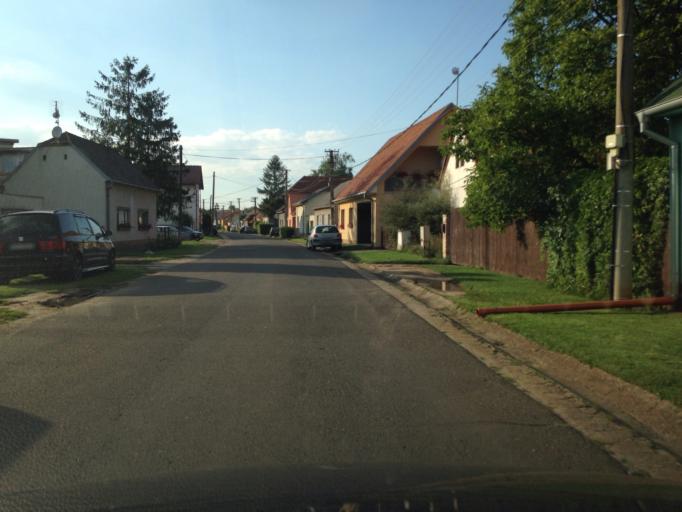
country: AT
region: Lower Austria
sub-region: Politischer Bezirk Ganserndorf
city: Angern an der March
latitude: 48.4041
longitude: 16.8601
